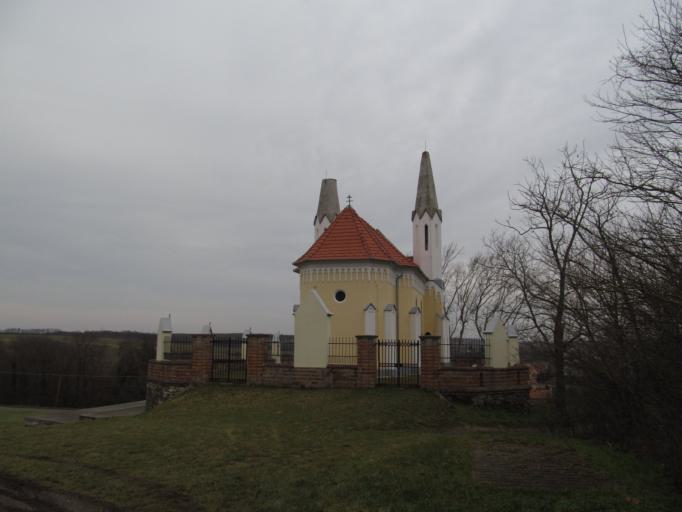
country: HU
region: Vas
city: Sarvar
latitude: 47.2377
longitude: 17.0127
